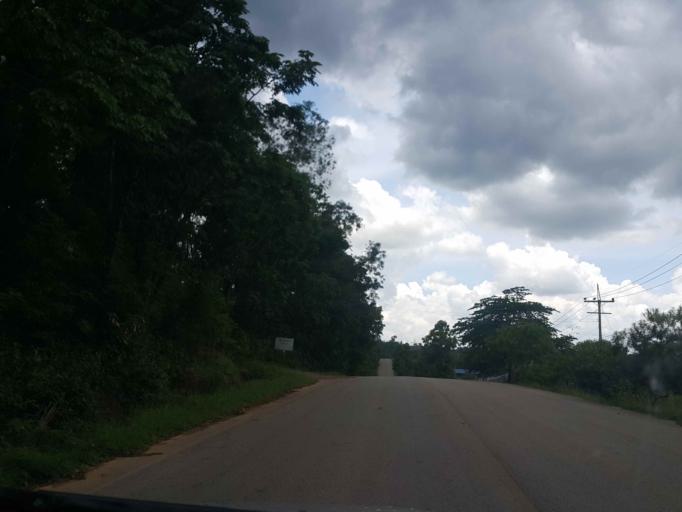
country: TH
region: Phayao
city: Dok Kham Tai
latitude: 18.9778
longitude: 100.0709
